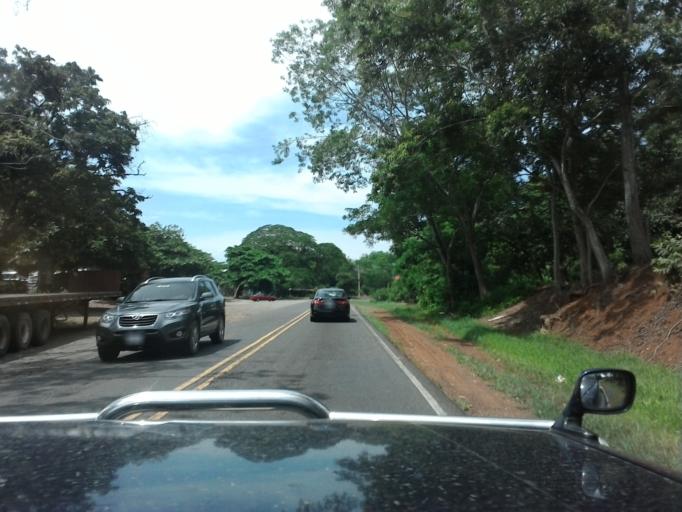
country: CR
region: Puntarenas
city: Esparza
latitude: 10.0057
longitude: -84.6186
